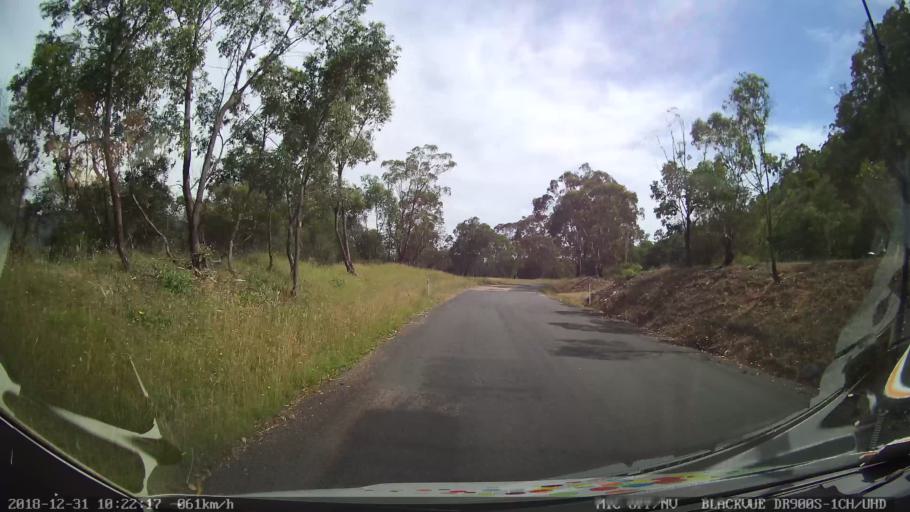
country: AU
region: New South Wales
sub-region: Snowy River
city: Jindabyne
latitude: -36.5269
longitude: 148.1428
